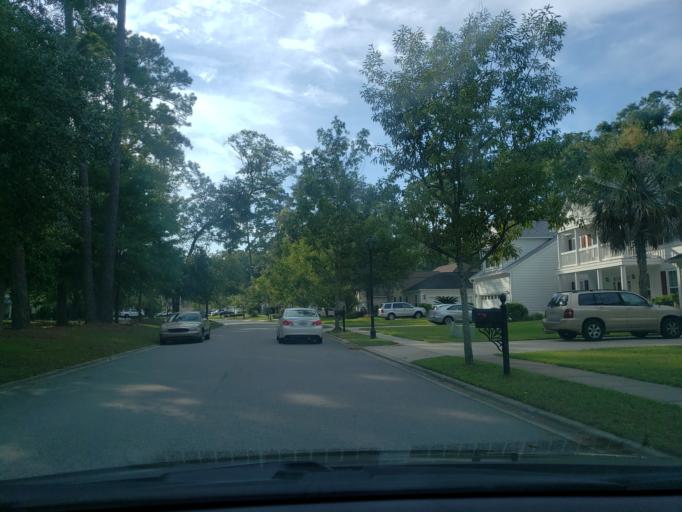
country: US
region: Georgia
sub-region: Chatham County
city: Montgomery
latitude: 31.9550
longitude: -81.1475
